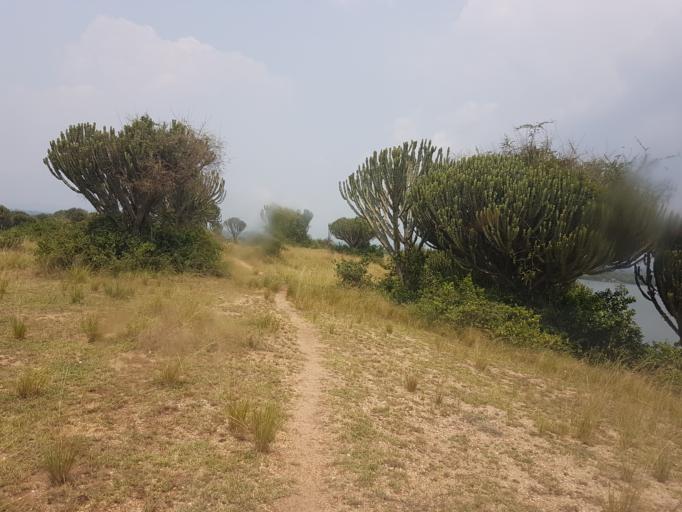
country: UG
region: Western Region
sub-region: Rubirizi District
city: Rubirizi
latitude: -0.0791
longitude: 30.1795
